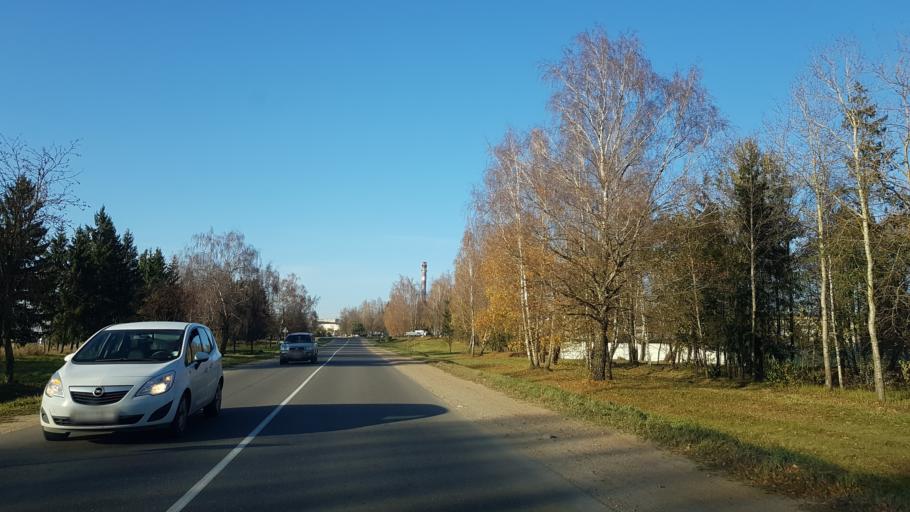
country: BY
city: Fanipol
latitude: 53.7311
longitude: 27.3326
